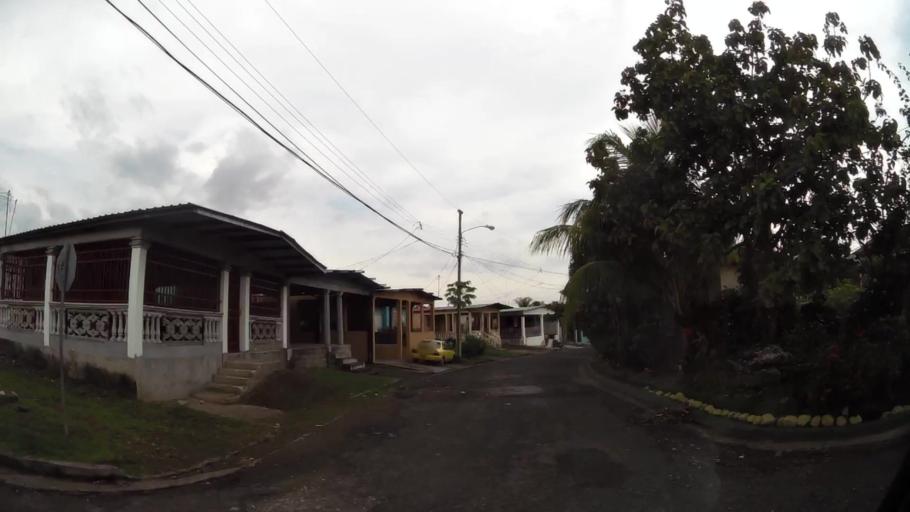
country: PA
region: Panama
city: Cabra Numero Uno
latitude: 9.0953
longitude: -79.3461
